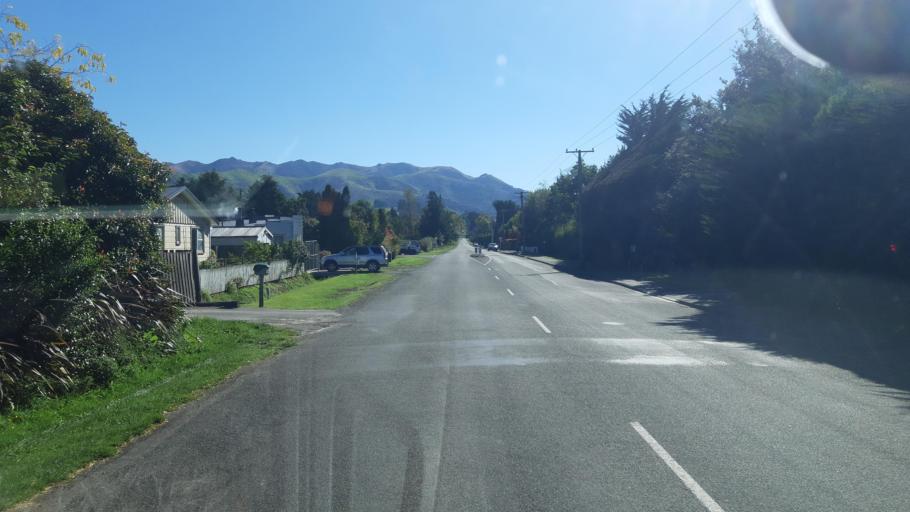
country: NZ
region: Canterbury
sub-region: Waimakariri District
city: Oxford
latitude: -43.2886
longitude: 172.1963
